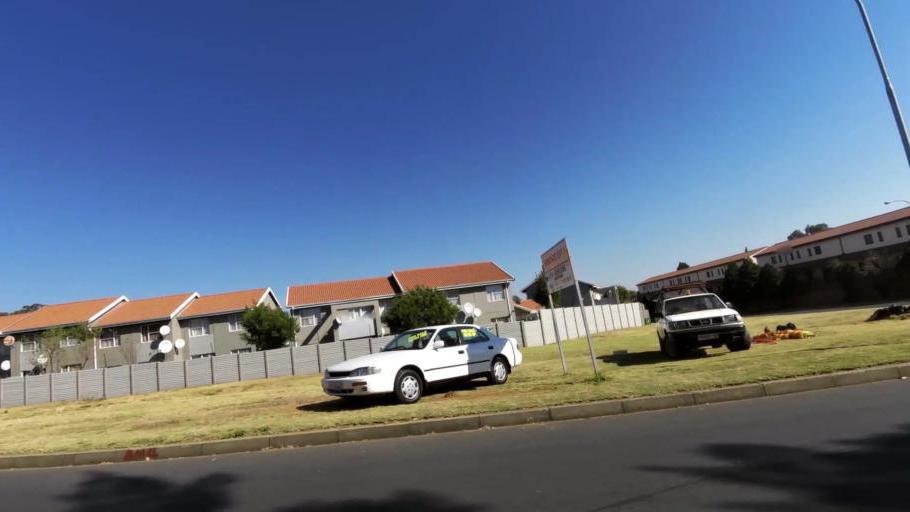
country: ZA
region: Gauteng
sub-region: City of Johannesburg Metropolitan Municipality
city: Johannesburg
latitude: -26.2465
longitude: 27.9982
